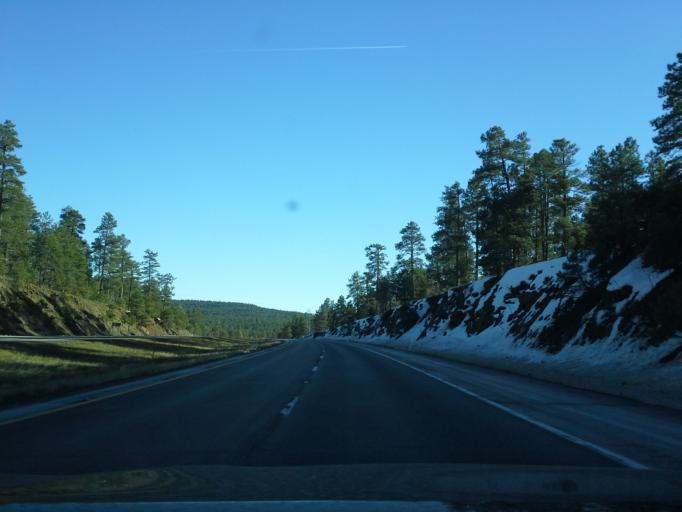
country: US
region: Arizona
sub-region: Coconino County
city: Kachina Village
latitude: 35.0789
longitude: -111.6868
